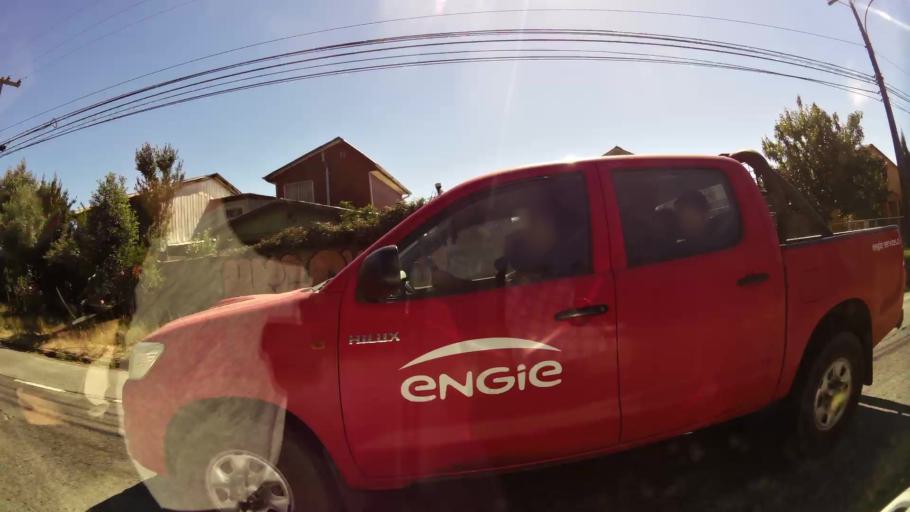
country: CL
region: Biobio
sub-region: Provincia de Concepcion
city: Concepcion
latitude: -36.8009
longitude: -73.0258
